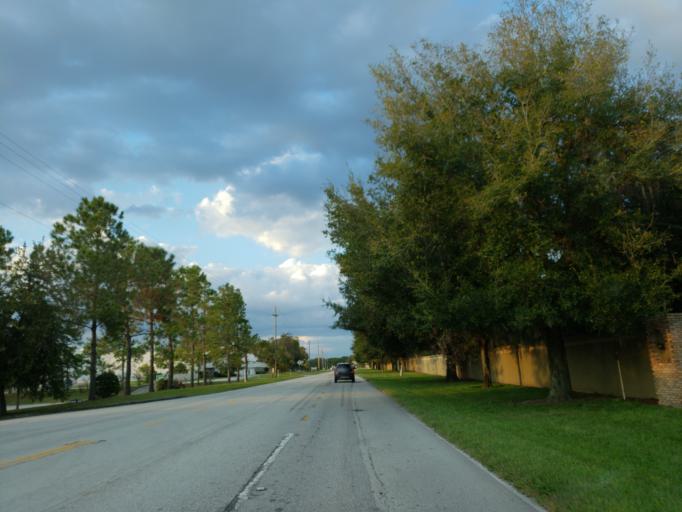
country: US
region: Florida
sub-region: Pasco County
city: Odessa
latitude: 28.1819
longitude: -82.5923
